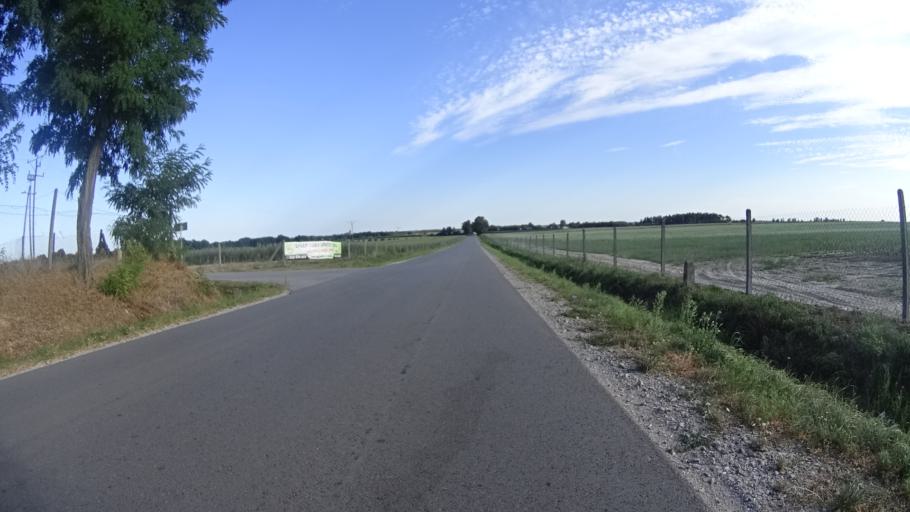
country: PL
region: Masovian Voivodeship
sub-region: Powiat grojecki
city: Goszczyn
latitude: 51.6816
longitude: 20.8255
